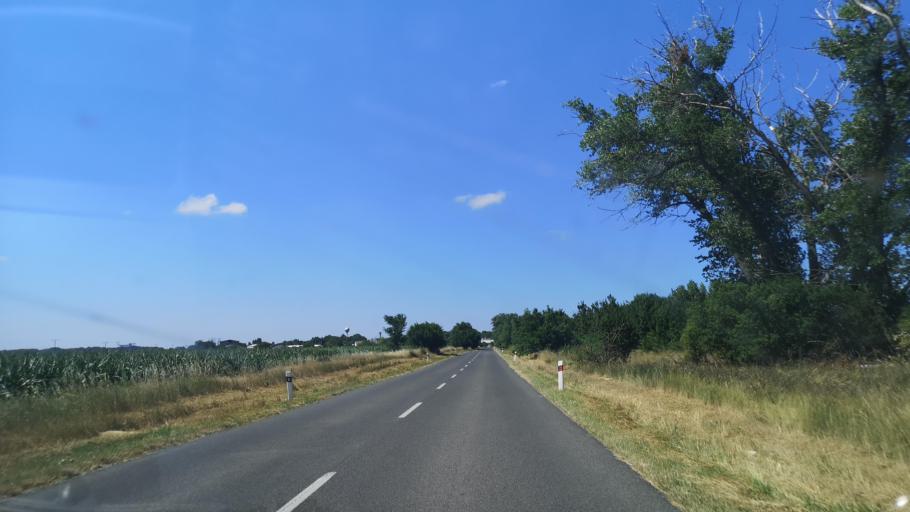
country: SK
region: Trnavsky
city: Dunajska Streda
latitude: 48.0629
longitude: 17.4743
